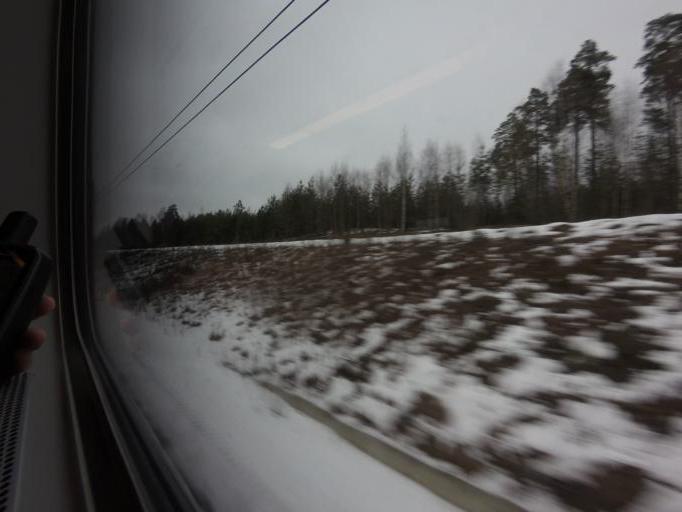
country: NO
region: Akershus
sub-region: Ullensaker
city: Jessheim
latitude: 60.1584
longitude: 11.1443
